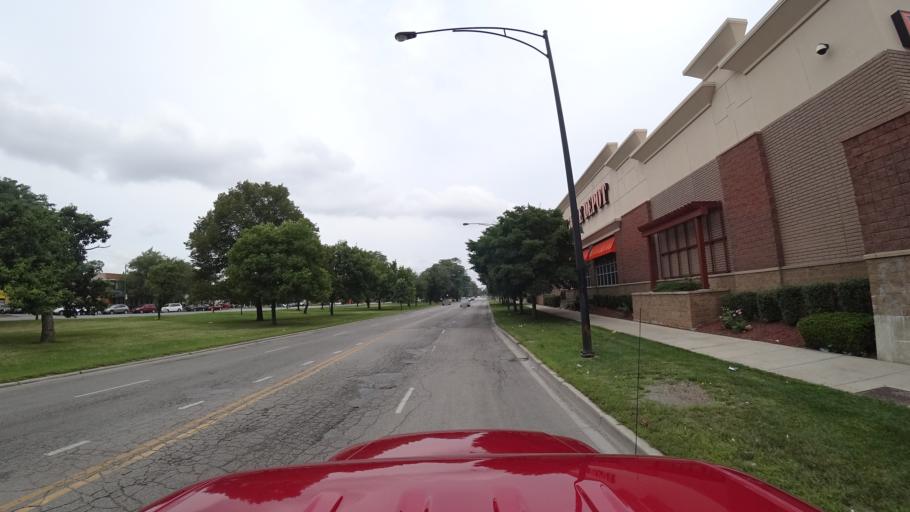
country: US
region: Illinois
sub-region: Cook County
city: Chicago
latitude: 41.8103
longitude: -87.6838
